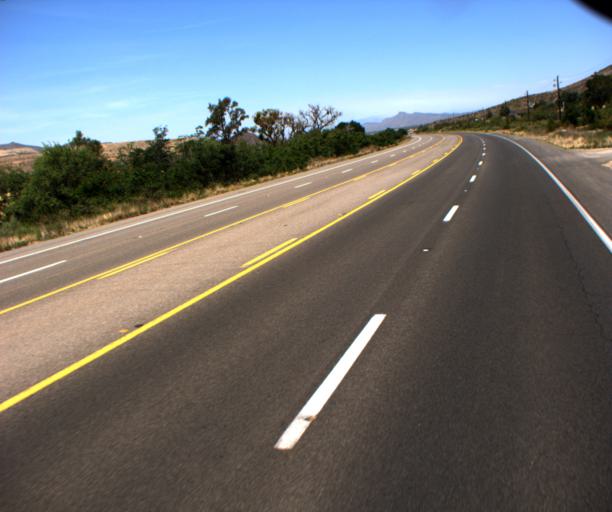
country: US
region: Arizona
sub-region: Gila County
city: Claypool
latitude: 33.4238
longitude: -110.8257
